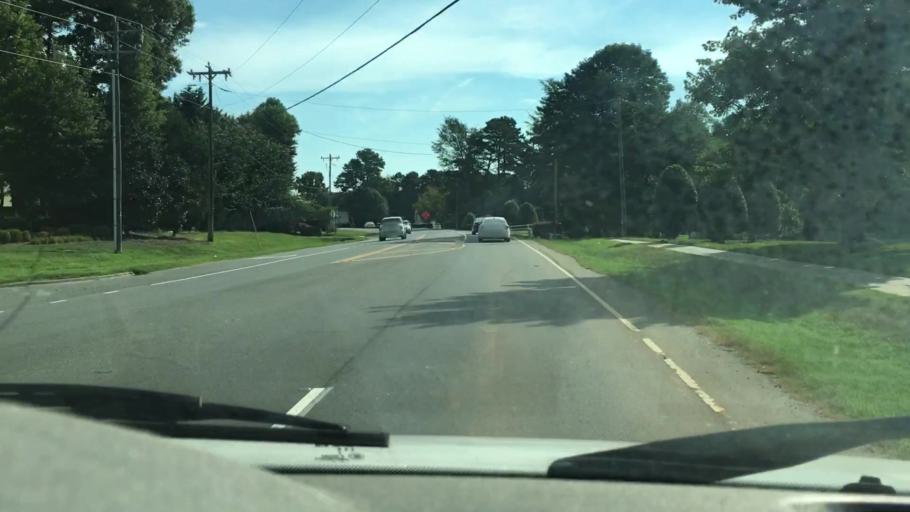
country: US
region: North Carolina
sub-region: Mecklenburg County
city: Huntersville
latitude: 35.3815
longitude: -80.7907
